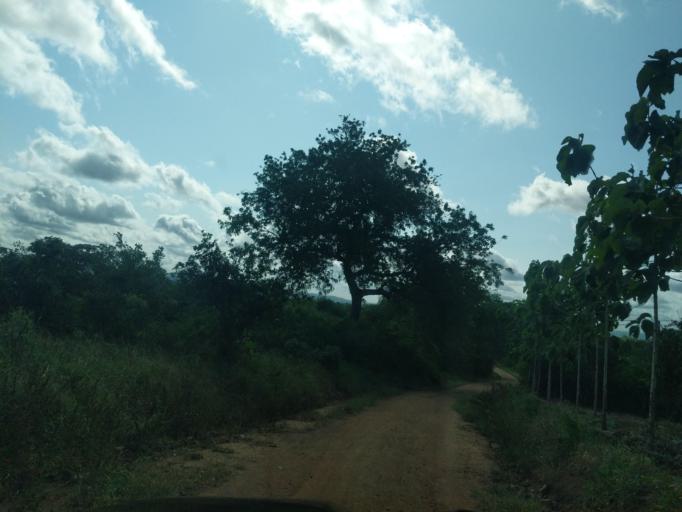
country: TZ
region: Tanga
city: Muheza
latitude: -5.4196
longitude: 38.6427
